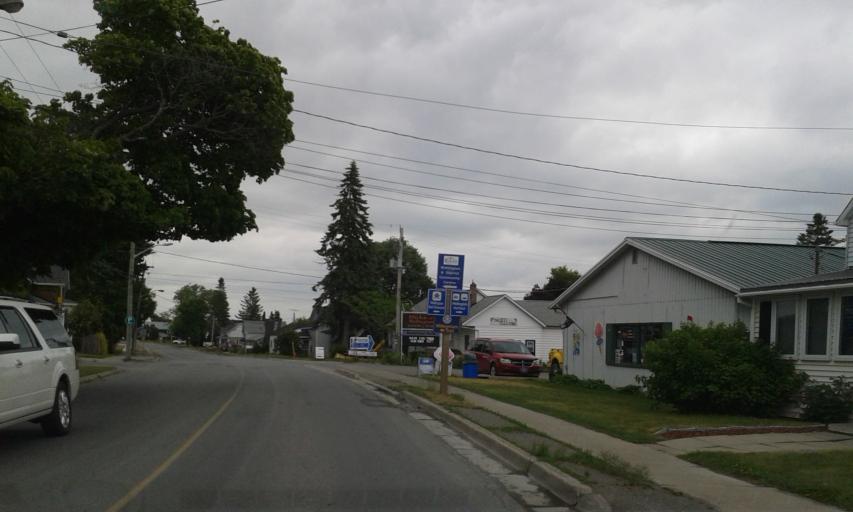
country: CA
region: Ontario
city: Prince Edward
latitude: 43.9521
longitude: -77.3396
